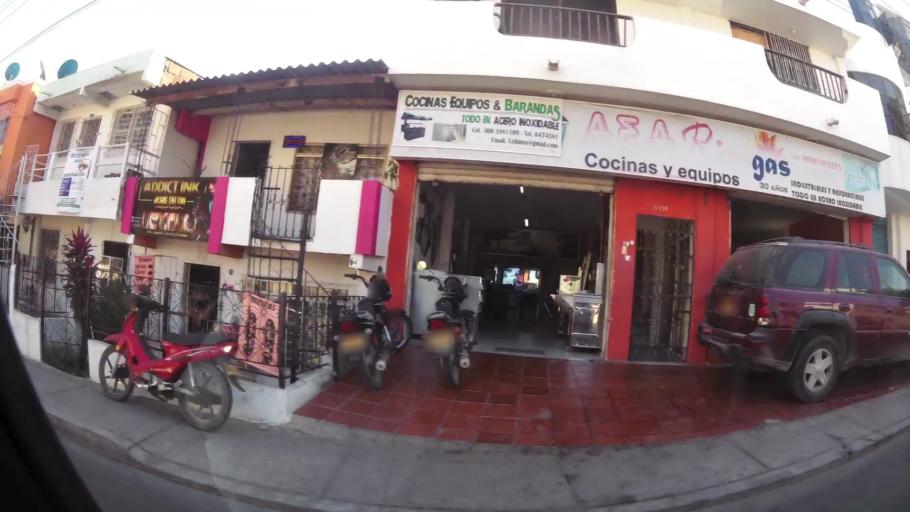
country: CO
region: Bolivar
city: Cartagena
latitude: 10.3968
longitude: -75.4957
